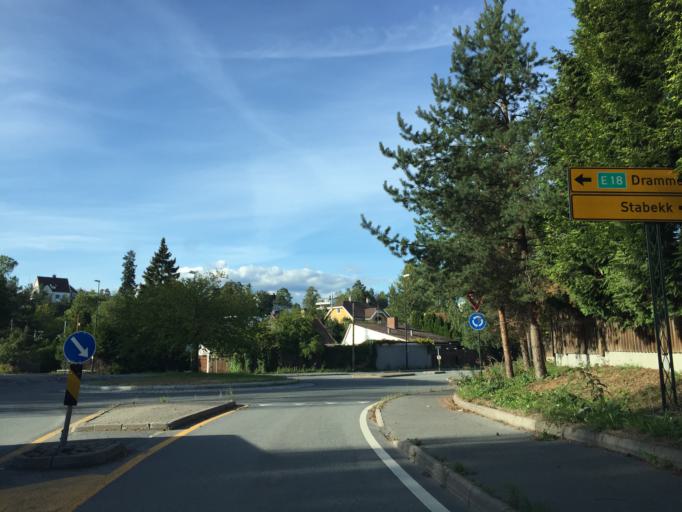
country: NO
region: Akershus
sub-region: Baerum
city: Lysaker
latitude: 59.9035
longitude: 10.5969
